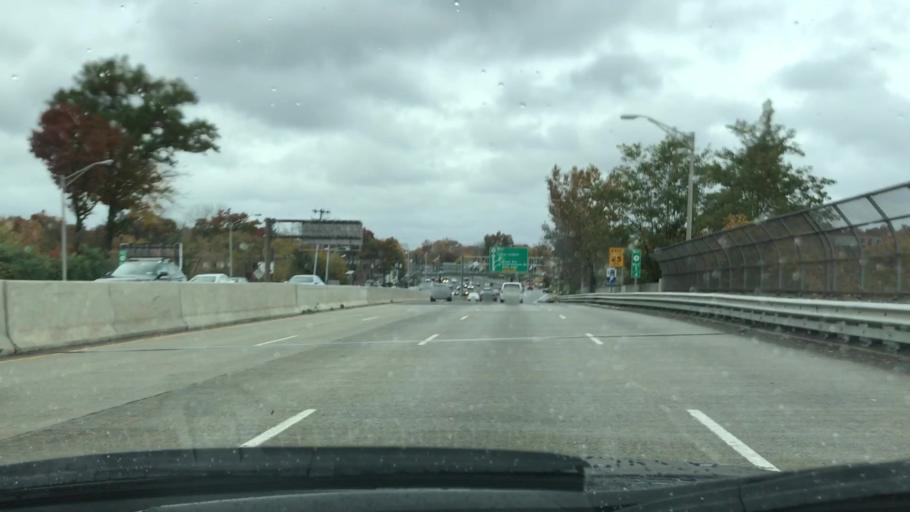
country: US
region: New Jersey
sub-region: Bergen County
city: River Edge
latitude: 40.9090
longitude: -74.0362
